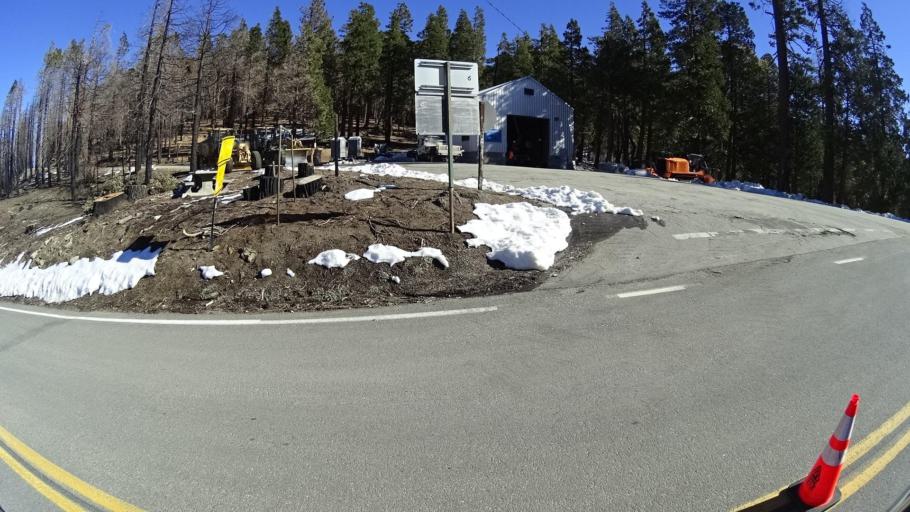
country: US
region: California
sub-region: Kern County
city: Alta Sierra
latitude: 35.7390
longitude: -118.5565
